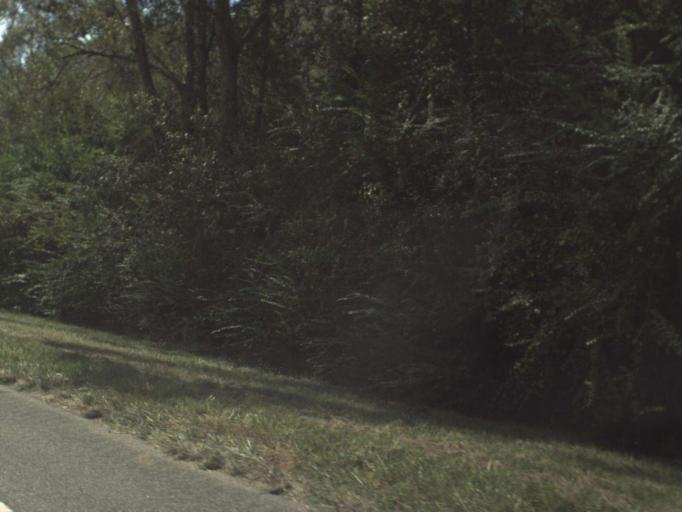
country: US
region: Florida
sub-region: Washington County
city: Chipley
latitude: 30.7073
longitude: -85.5598
